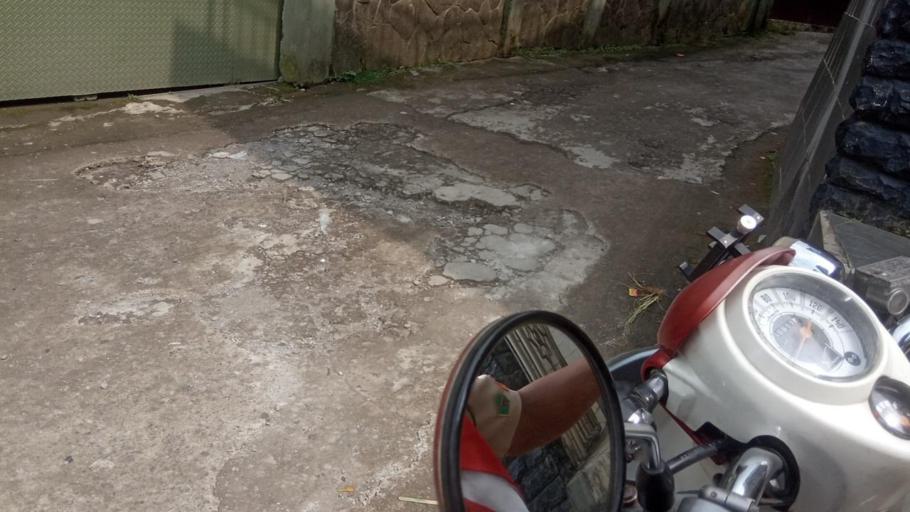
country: ID
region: West Java
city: Caringin
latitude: -6.6510
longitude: 106.9020
